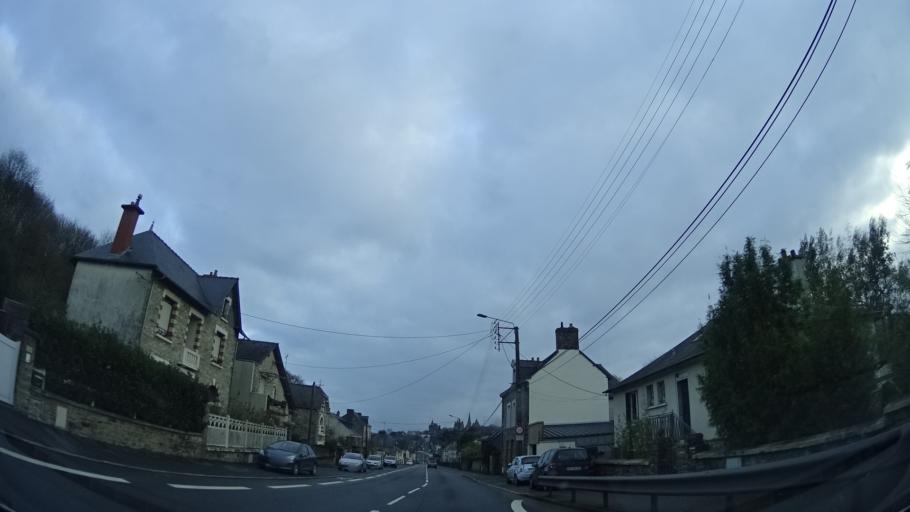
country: FR
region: Brittany
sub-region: Departement d'Ille-et-Vilaine
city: Vitre
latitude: 48.1218
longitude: -1.2257
